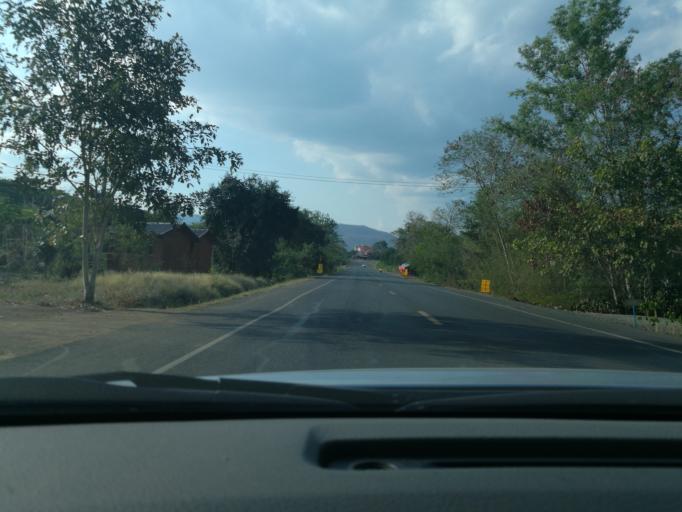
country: TH
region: Phetchabun
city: Phetchabun
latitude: 16.5446
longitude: 101.1437
